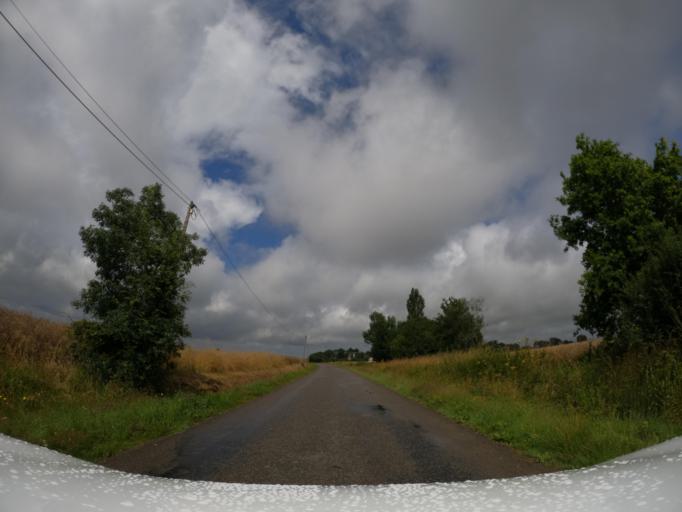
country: FR
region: Pays de la Loire
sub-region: Departement de la Loire-Atlantique
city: Ligne
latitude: 47.3983
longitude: -1.3876
